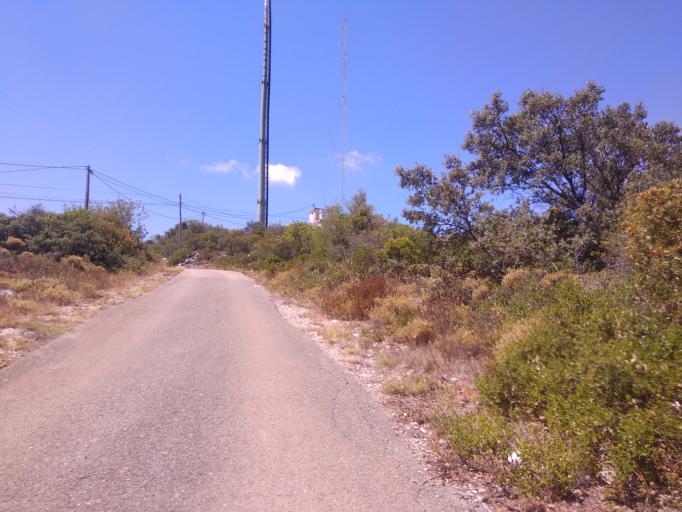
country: PT
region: Faro
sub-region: Sao Bras de Alportel
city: Sao Bras de Alportel
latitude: 37.1604
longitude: -7.9045
